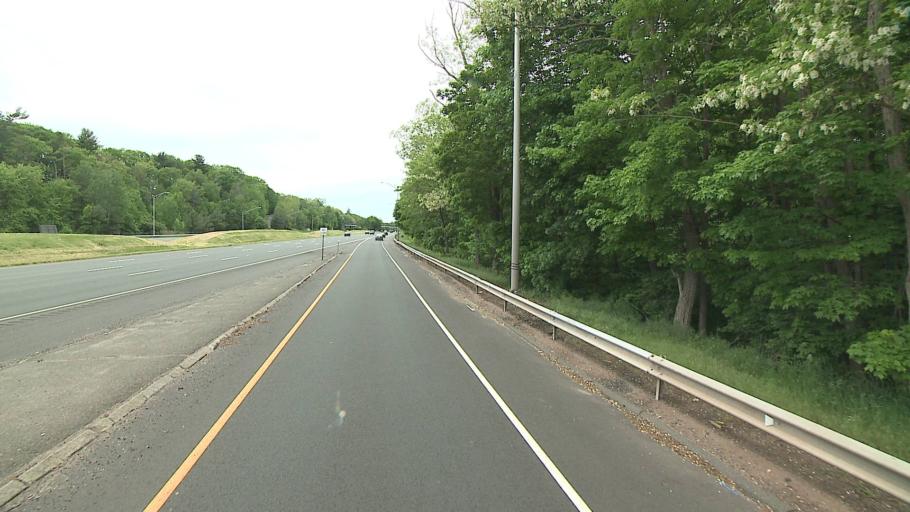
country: US
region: Connecticut
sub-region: Hartford County
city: Manchester
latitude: 41.7630
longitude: -72.5245
